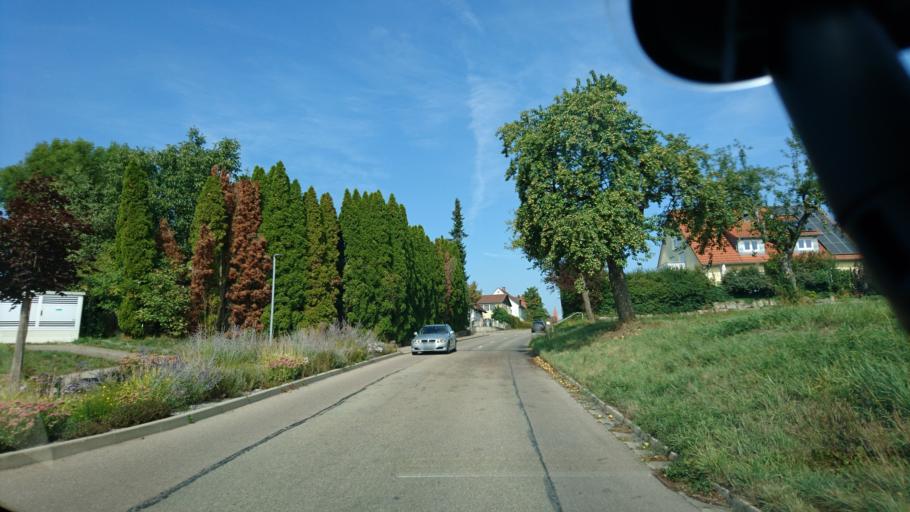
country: DE
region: Baden-Wuerttemberg
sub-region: Regierungsbezirk Stuttgart
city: Ilshofen
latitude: 49.1657
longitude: 9.9232
